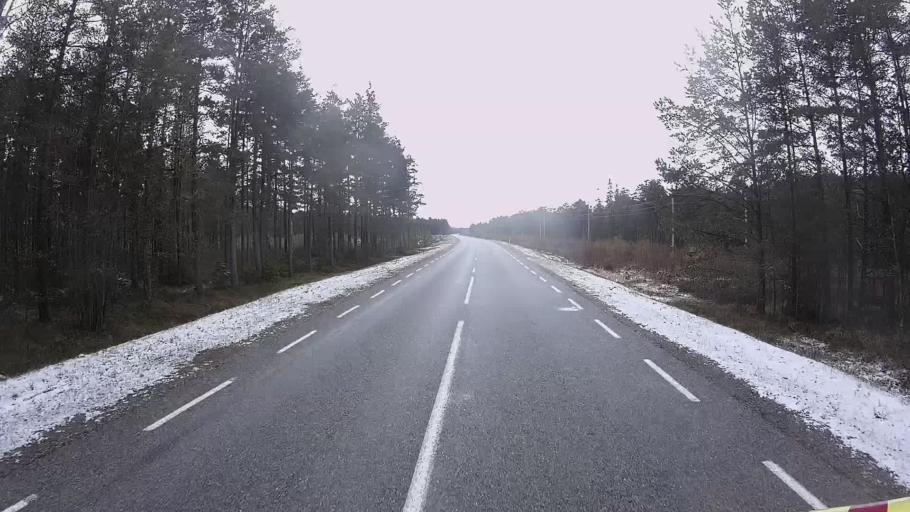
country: EE
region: Hiiumaa
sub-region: Kaerdla linn
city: Kardla
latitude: 59.0272
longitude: 22.6722
